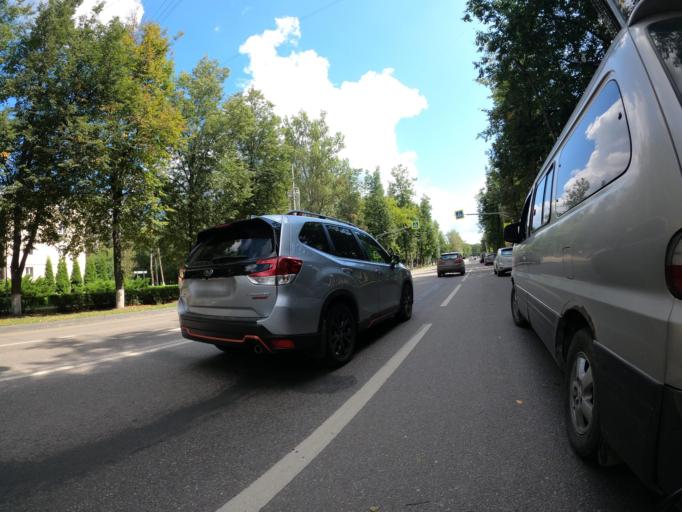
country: RU
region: Moskovskaya
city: Voskresensk
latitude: 55.3230
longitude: 38.6640
